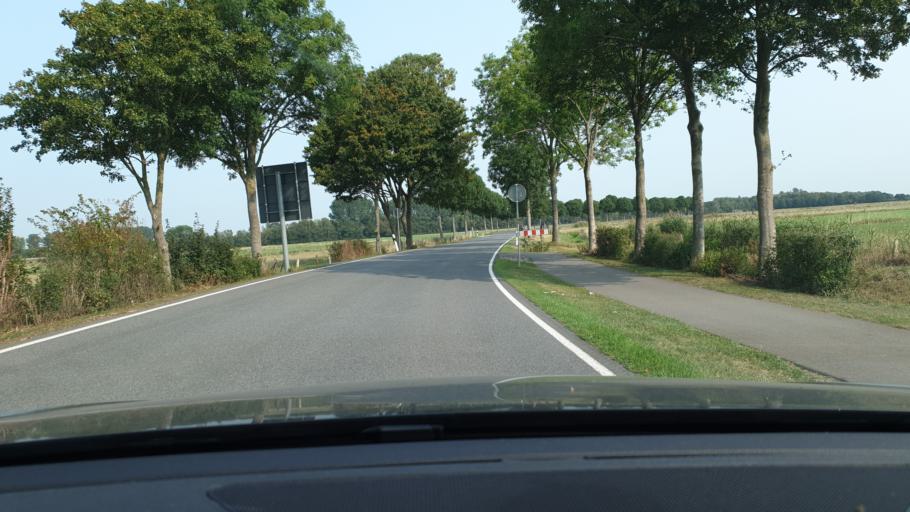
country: DE
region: North Rhine-Westphalia
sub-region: Regierungsbezirk Dusseldorf
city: Kranenburg
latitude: 51.7954
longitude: 6.0066
